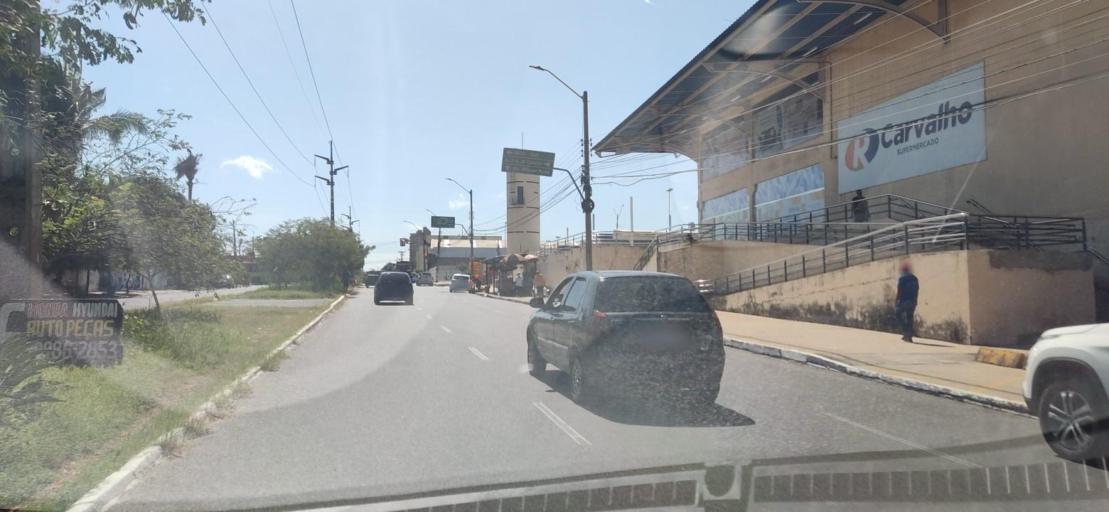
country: BR
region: Piaui
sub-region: Teresina
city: Teresina
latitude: -5.1201
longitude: -42.8041
